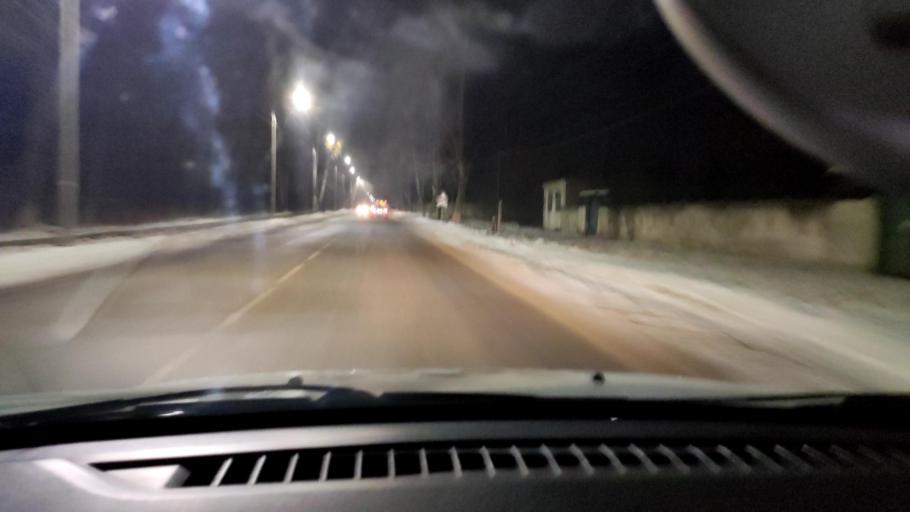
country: RU
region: Perm
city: Kultayevo
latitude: 57.9806
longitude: 55.9172
